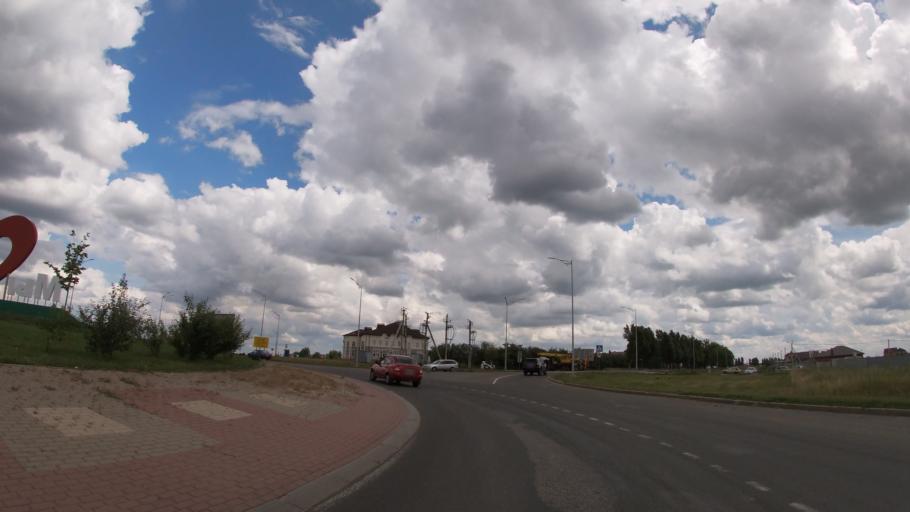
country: RU
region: Belgorod
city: Mayskiy
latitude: 50.5263
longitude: 36.5191
